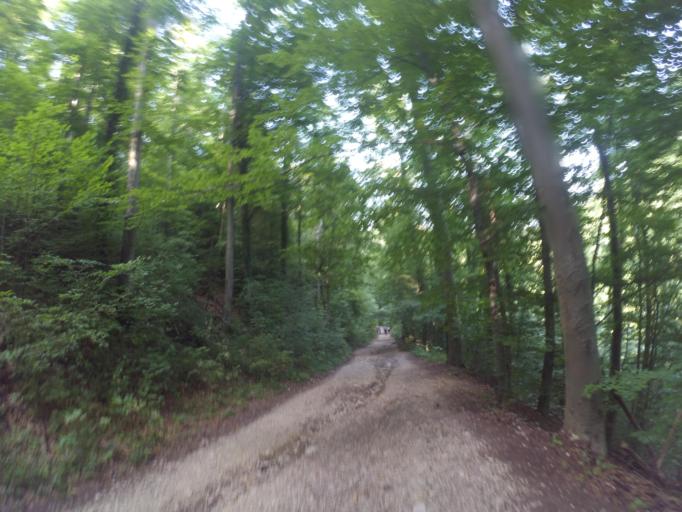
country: DE
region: Baden-Wuerttemberg
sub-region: Tuebingen Region
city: Bad Urach
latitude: 48.4905
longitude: 9.3810
